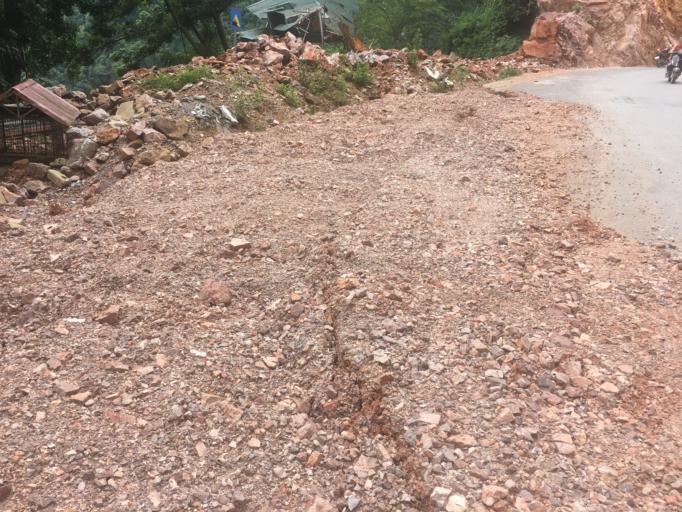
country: VN
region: Ha Giang
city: Thanh Pho Ha Giang
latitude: 22.8512
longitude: 105.0166
